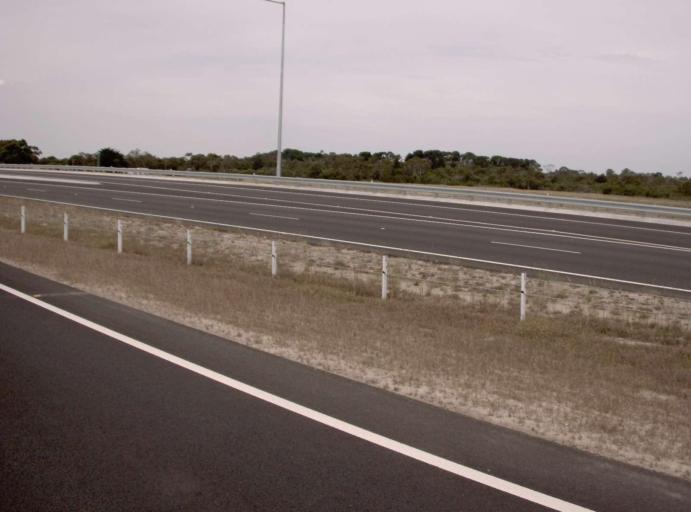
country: AU
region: Victoria
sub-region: Mornington Peninsula
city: Baxter
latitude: -38.1987
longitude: 145.1458
